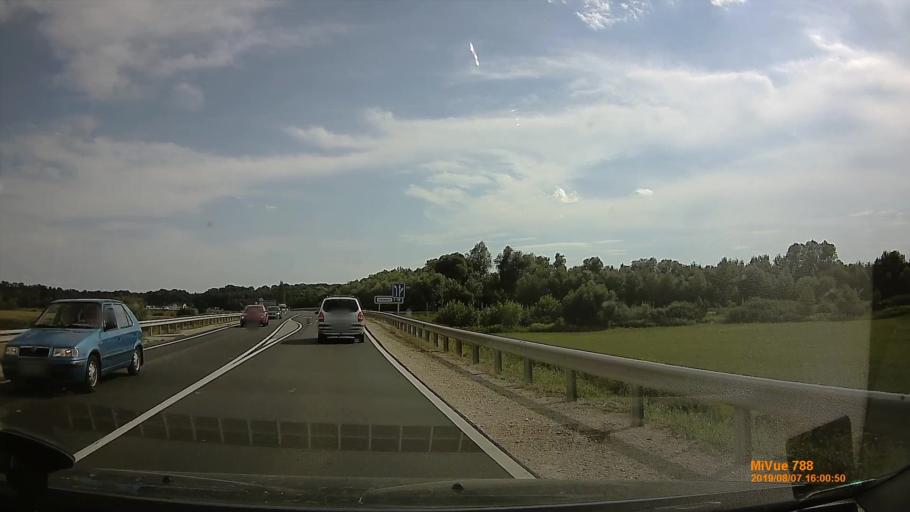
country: HU
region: Vas
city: Kormend
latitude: 46.9969
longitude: 16.6153
